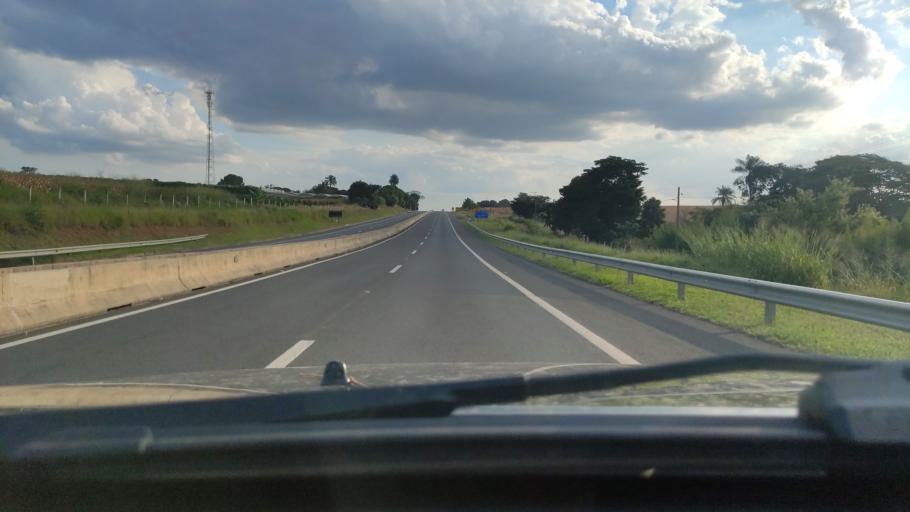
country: BR
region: Sao Paulo
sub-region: Artur Nogueira
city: Artur Nogueira
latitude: -22.4636
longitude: -47.1046
